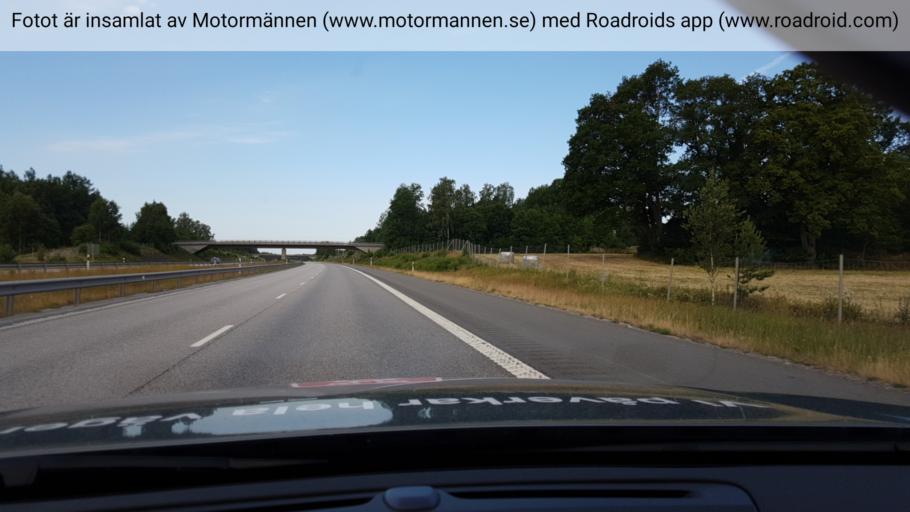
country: SE
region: OErebro
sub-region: Lindesbergs Kommun
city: Fellingsbro
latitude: 59.3299
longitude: 15.5123
